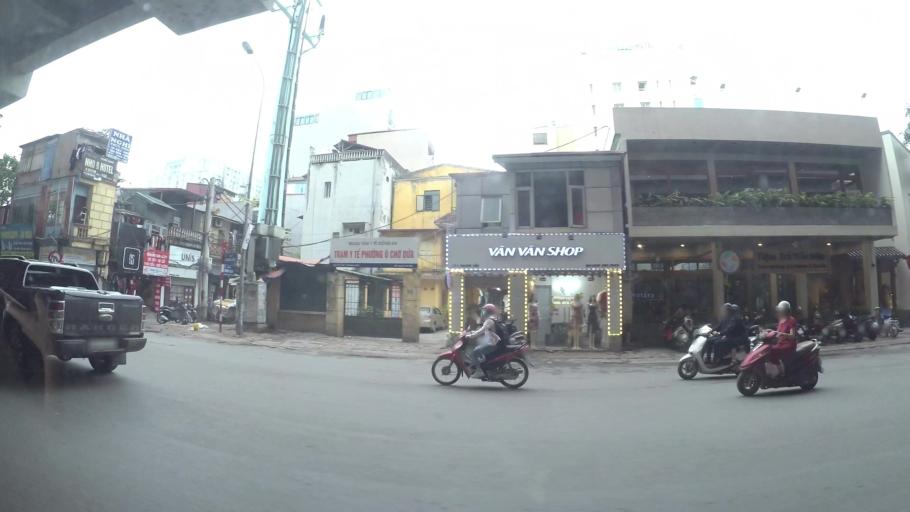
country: VN
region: Ha Noi
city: Dong Da
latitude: 21.0203
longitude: 105.8255
